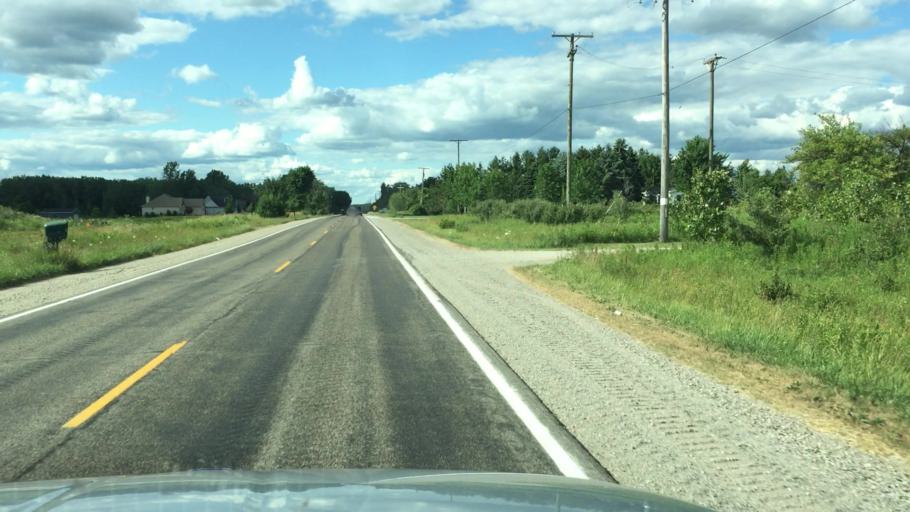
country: US
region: Michigan
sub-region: Saint Clair County
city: Capac
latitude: 43.0617
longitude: -82.9299
